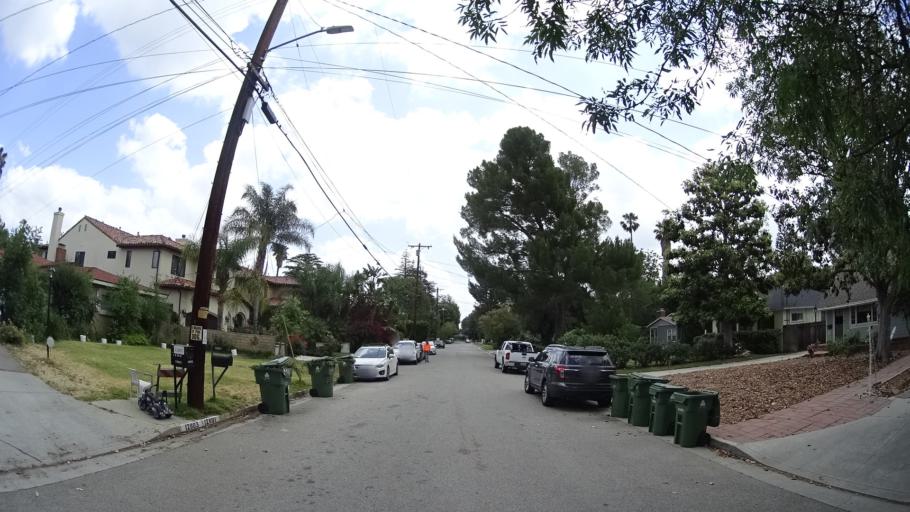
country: US
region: California
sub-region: Los Angeles County
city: Sherman Oaks
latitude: 34.1518
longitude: -118.4118
